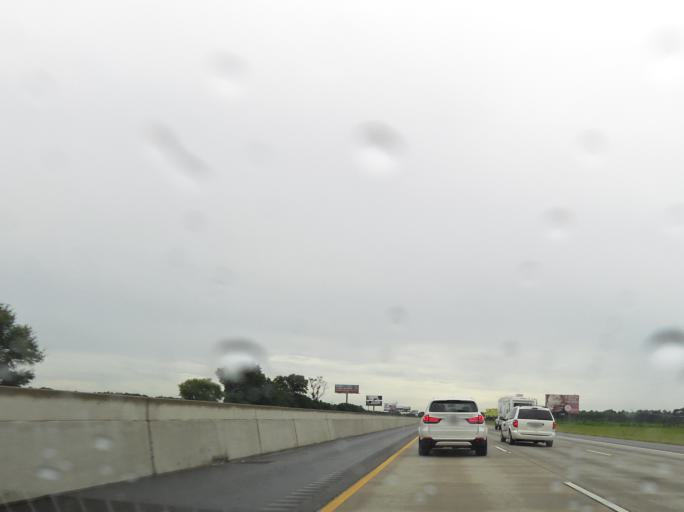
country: US
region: Georgia
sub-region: Cook County
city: Sparks
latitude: 31.1804
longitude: -83.4529
